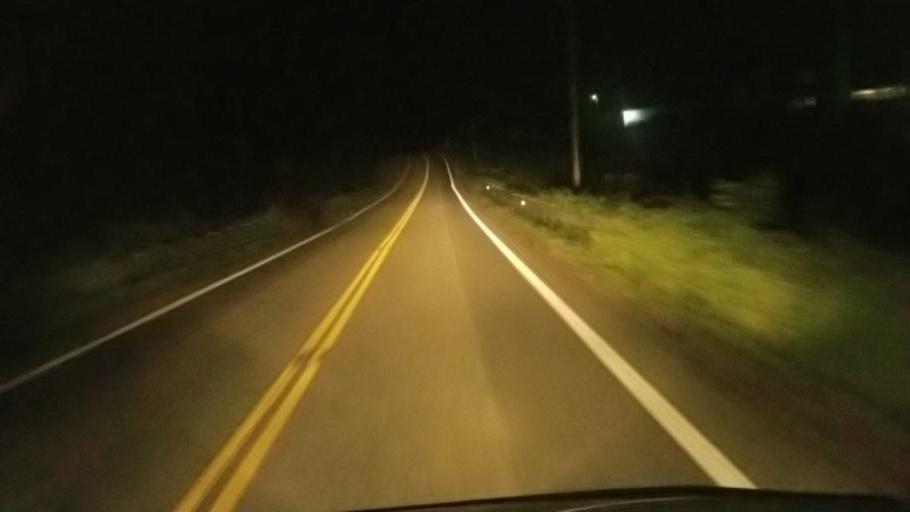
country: US
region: Ohio
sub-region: Ashland County
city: Loudonville
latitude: 40.5861
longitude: -82.1268
